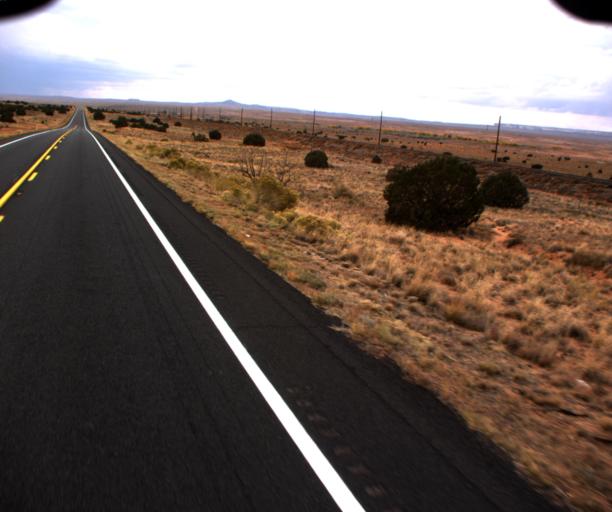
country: US
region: Arizona
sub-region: Coconino County
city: Kaibito
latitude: 36.4093
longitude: -110.8316
